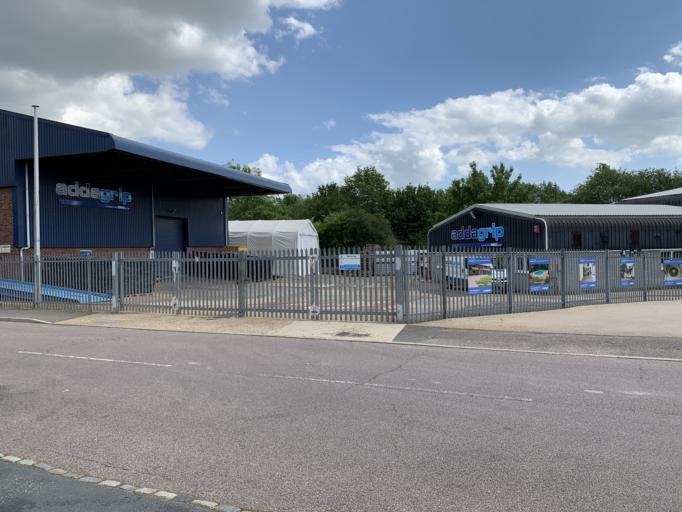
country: GB
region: England
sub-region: East Sussex
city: Uckfield
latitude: 50.9690
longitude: 0.0859
